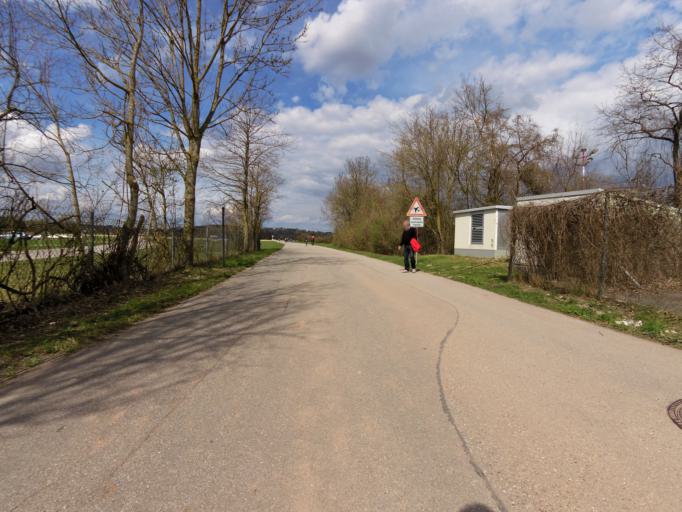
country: DE
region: Bavaria
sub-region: Lower Bavaria
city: Eching
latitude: 48.5120
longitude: 12.0419
